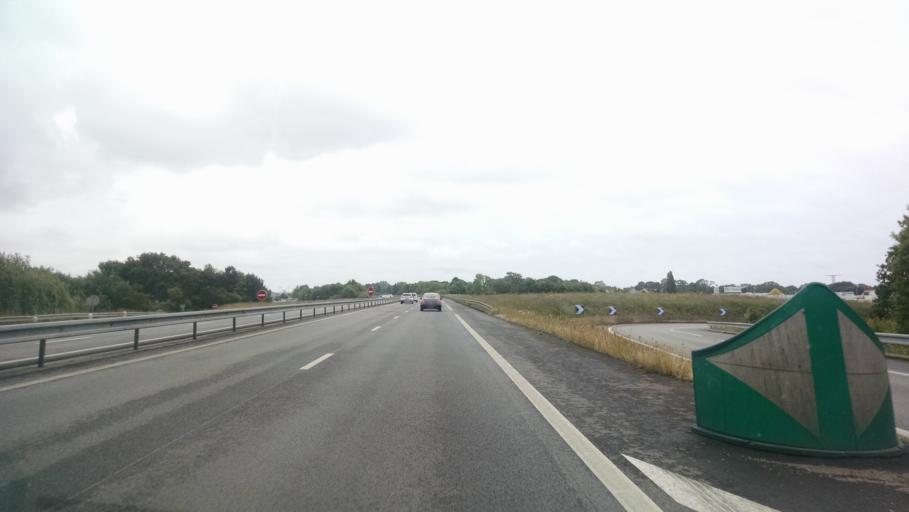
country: FR
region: Brittany
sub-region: Departement du Morbihan
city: Auray
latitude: 47.6665
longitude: -3.0115
